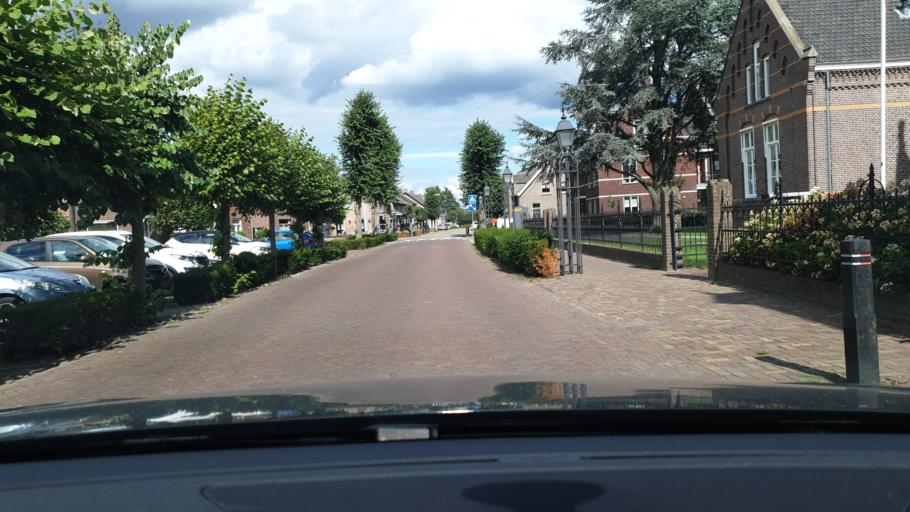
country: NL
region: North Brabant
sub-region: Gemeente Veghel
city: Zijtaart
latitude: 51.5927
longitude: 5.5416
